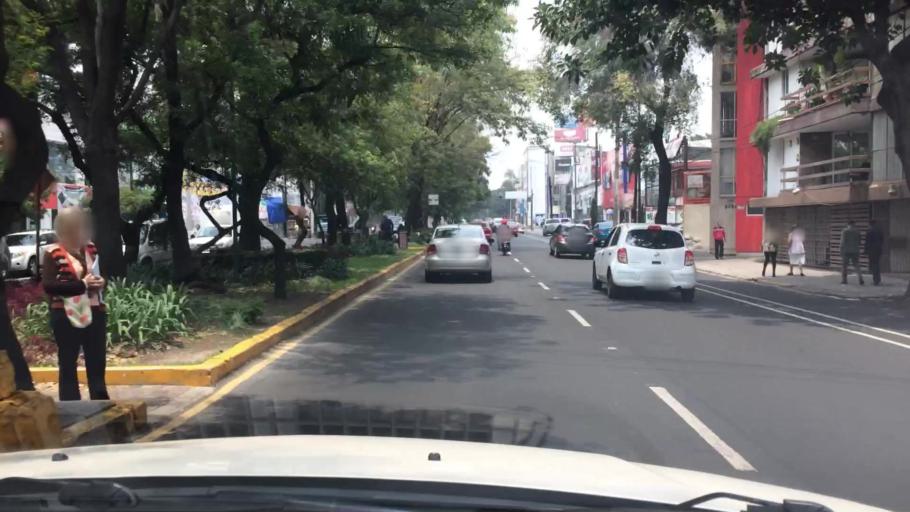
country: MX
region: Mexico City
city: Coyoacan
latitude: 19.3647
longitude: -99.1551
